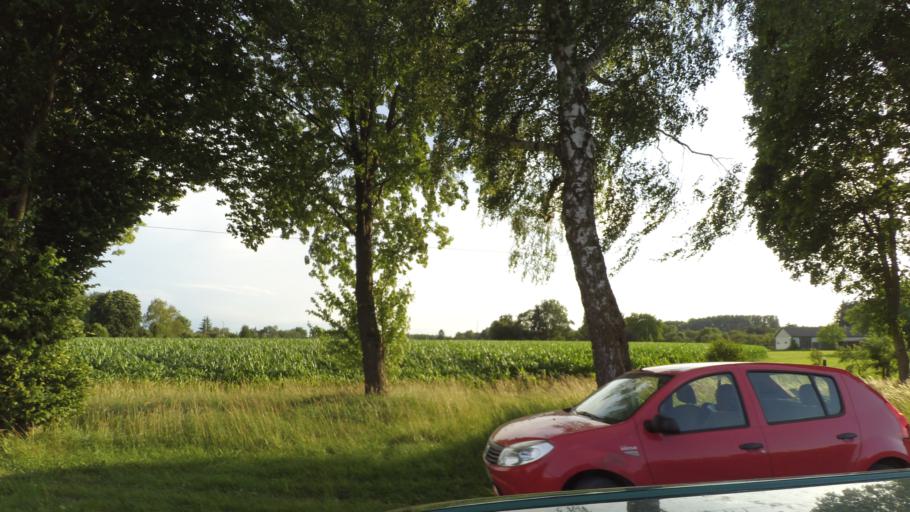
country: DE
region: Bavaria
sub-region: Swabia
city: Lauingen
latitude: 48.5653
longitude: 10.4412
